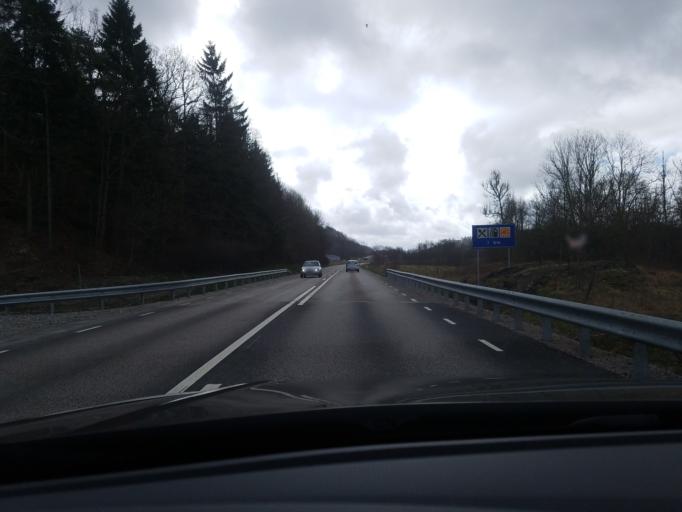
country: SE
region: Vaestra Goetaland
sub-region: Tjorns Kommun
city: Myggenas
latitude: 58.1346
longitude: 11.7166
